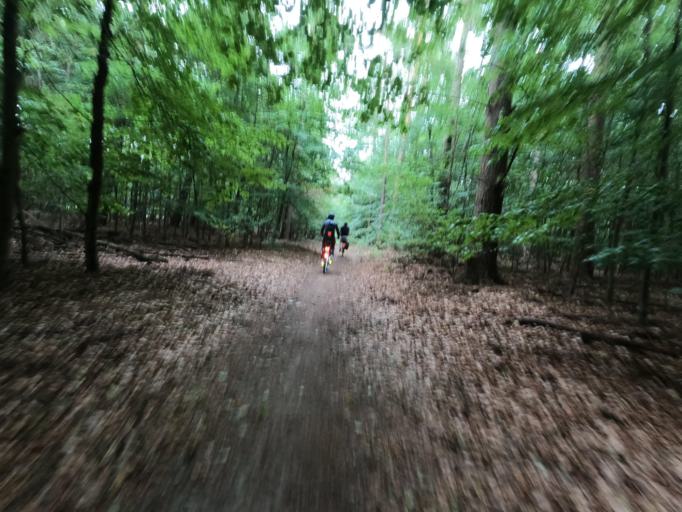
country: DE
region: North Rhine-Westphalia
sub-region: Regierungsbezirk Dusseldorf
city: Niederkruchten
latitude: 51.1790
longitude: 6.1779
